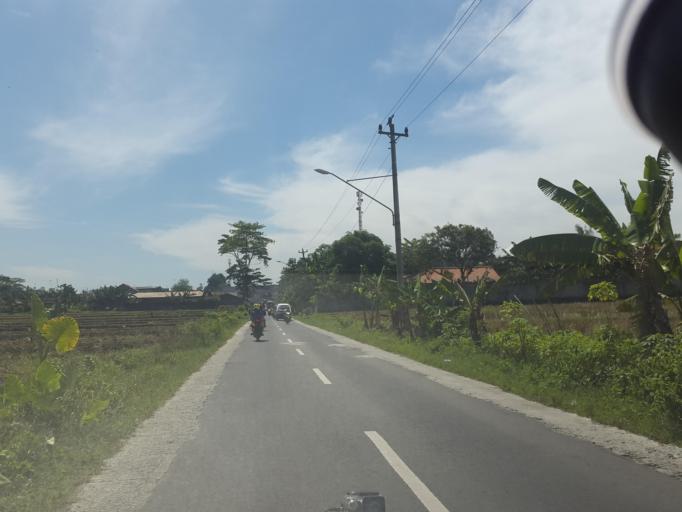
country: ID
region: Central Java
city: Sangkalputung
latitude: -7.4059
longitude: 109.0718
